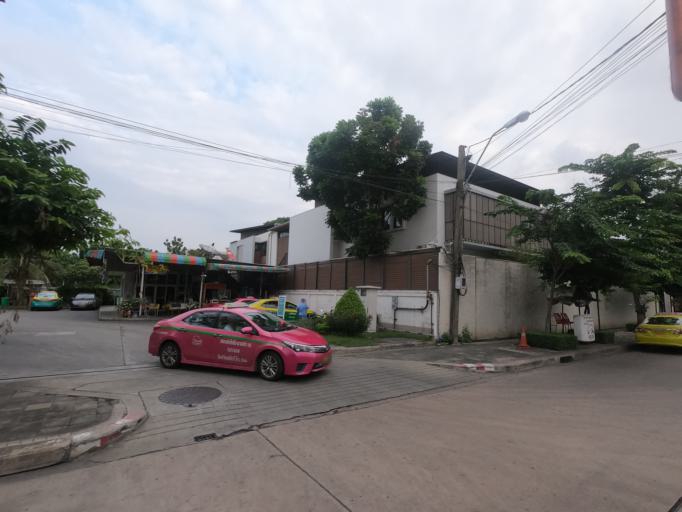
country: TH
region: Bangkok
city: Wang Thonglang
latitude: 13.7909
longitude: 100.6084
